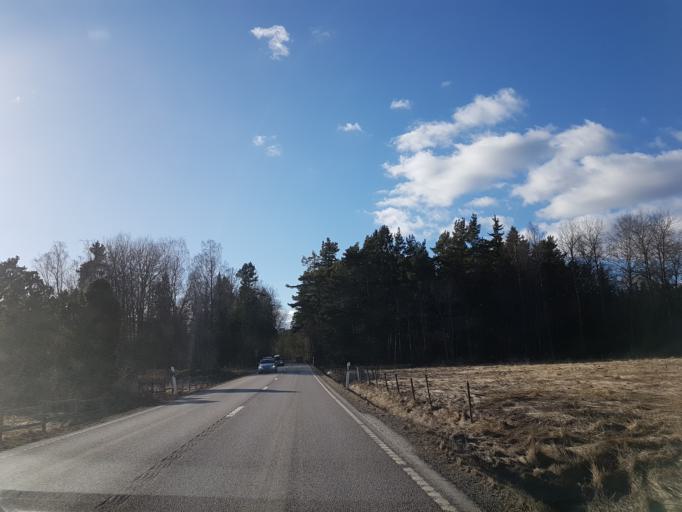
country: SE
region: Stockholm
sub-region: Norrtalje Kommun
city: Rimbo
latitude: 59.7371
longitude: 18.4747
